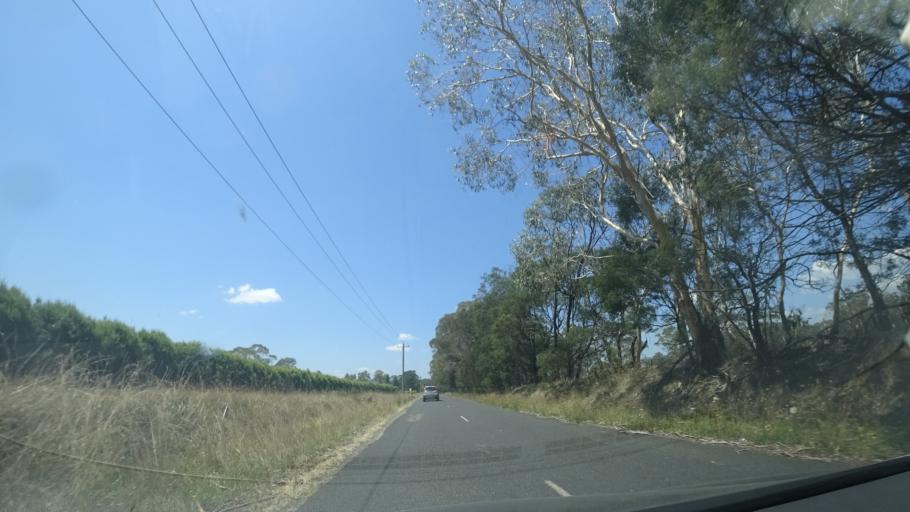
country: AU
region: New South Wales
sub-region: Wingecarribee
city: Bundanoon
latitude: -34.6107
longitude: 150.2620
